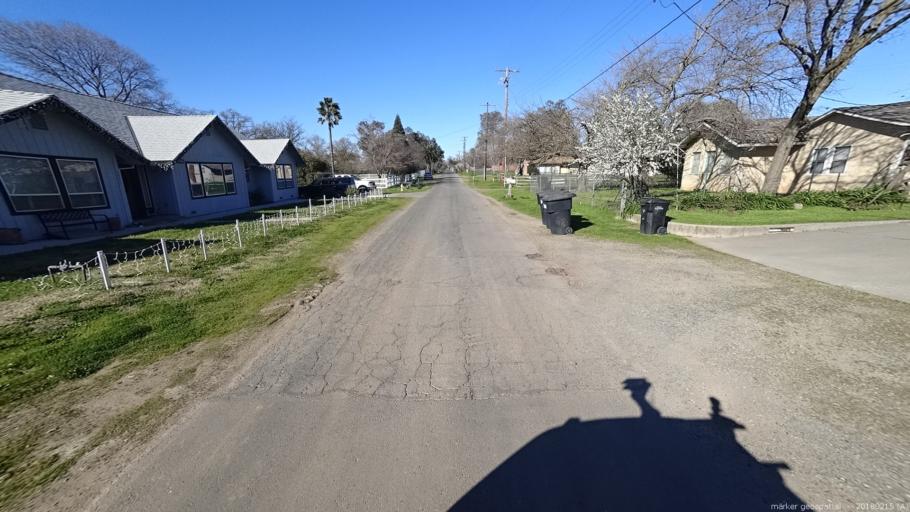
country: US
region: California
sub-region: Sacramento County
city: Rio Linda
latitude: 38.6709
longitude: -121.4615
